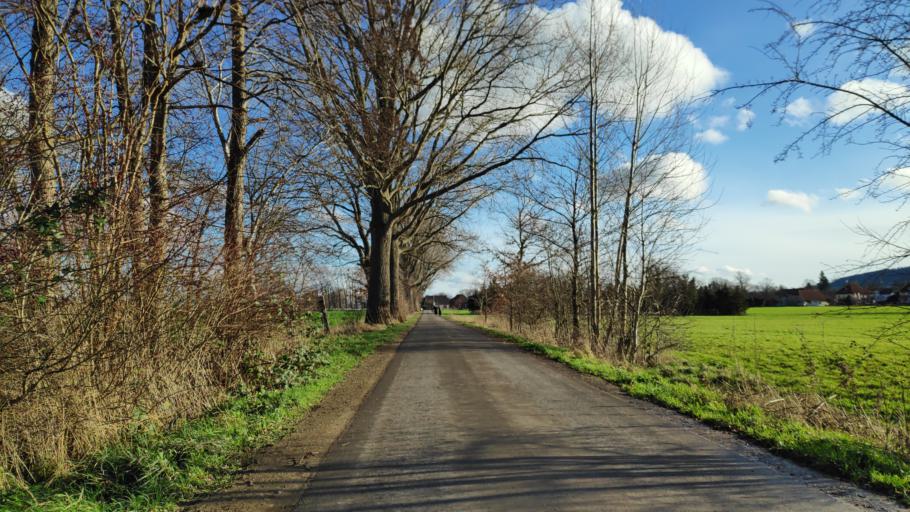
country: DE
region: North Rhine-Westphalia
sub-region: Regierungsbezirk Detmold
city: Minden
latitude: 52.2756
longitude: 8.8589
